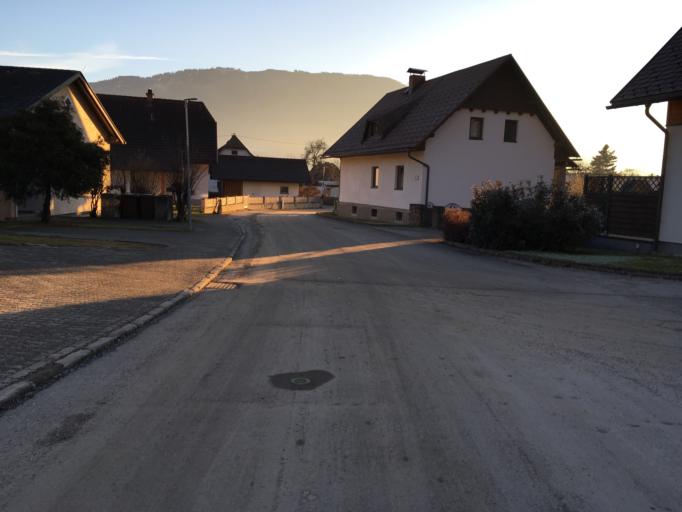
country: AT
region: Styria
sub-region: Politischer Bezirk Liezen
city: Weissenbach bei Liezen
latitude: 47.5709
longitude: 14.2035
